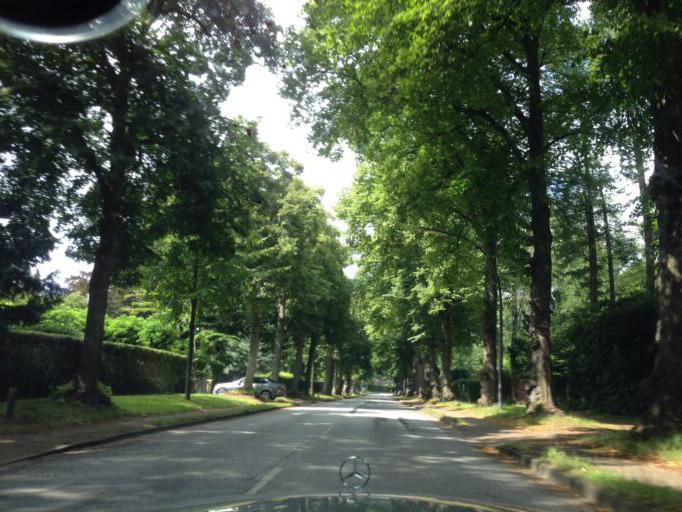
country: DE
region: Hamburg
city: Wohldorf-Ohlstedt
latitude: 53.6877
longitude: 10.1314
